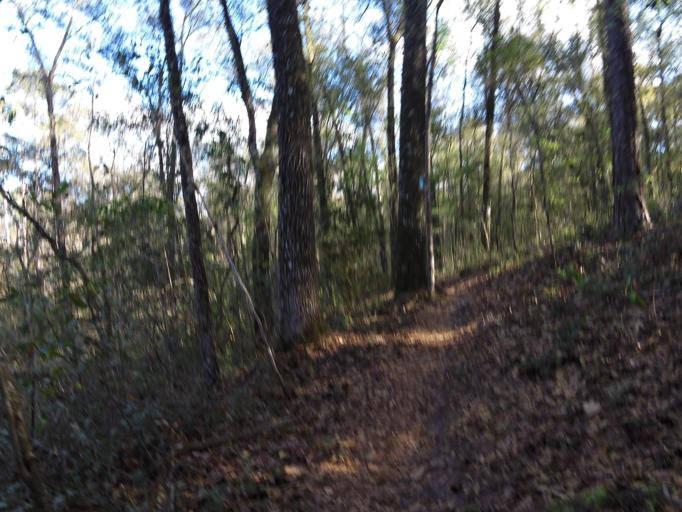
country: US
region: Florida
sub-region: Clay County
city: Middleburg
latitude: 30.1526
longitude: -81.9566
